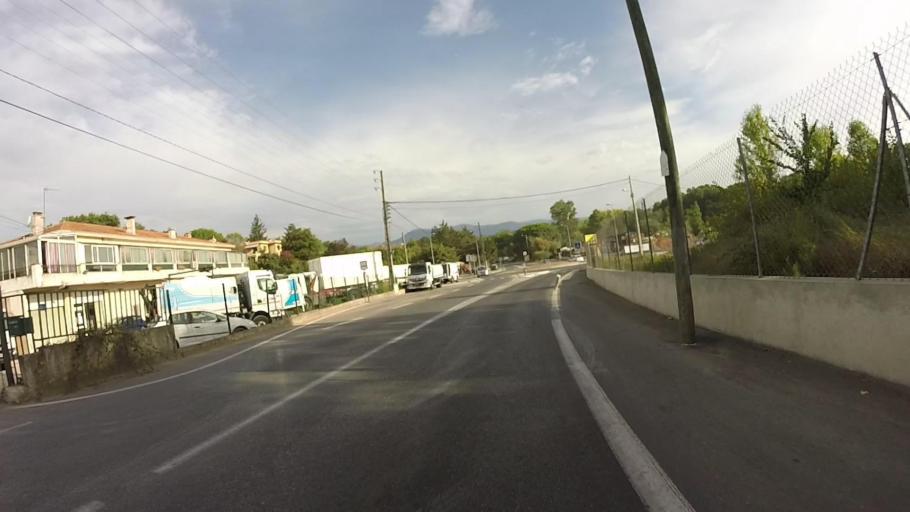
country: FR
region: Provence-Alpes-Cote d'Azur
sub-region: Departement des Alpes-Maritimes
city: Biot
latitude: 43.6070
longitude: 7.1116
